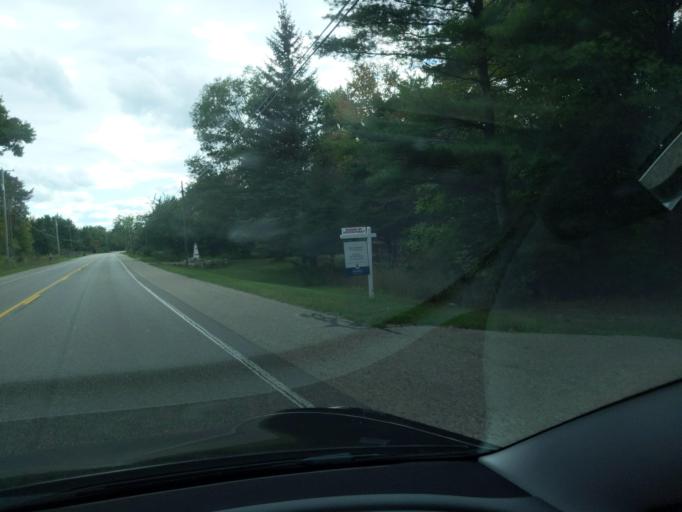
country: US
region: Michigan
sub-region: Kalkaska County
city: Rapid City
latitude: 44.8672
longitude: -85.2785
